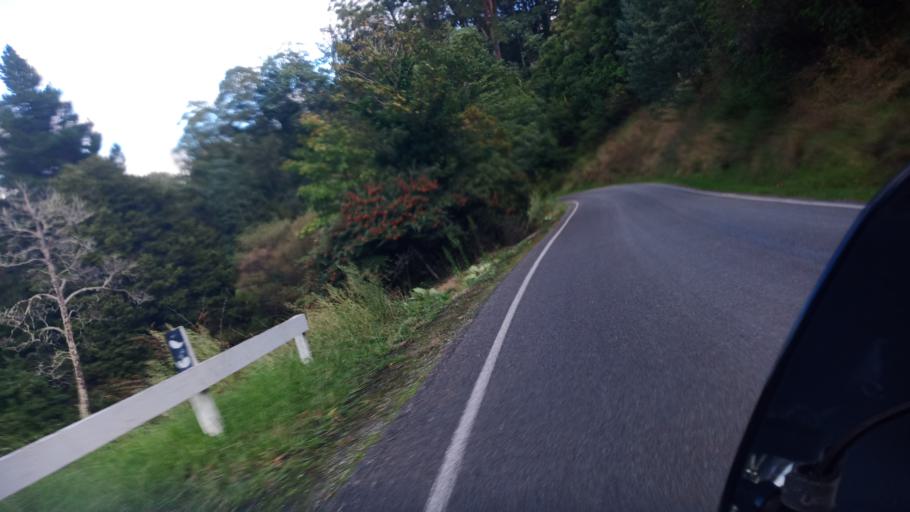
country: NZ
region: Gisborne
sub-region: Gisborne District
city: Gisborne
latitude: -38.5325
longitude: 177.5356
